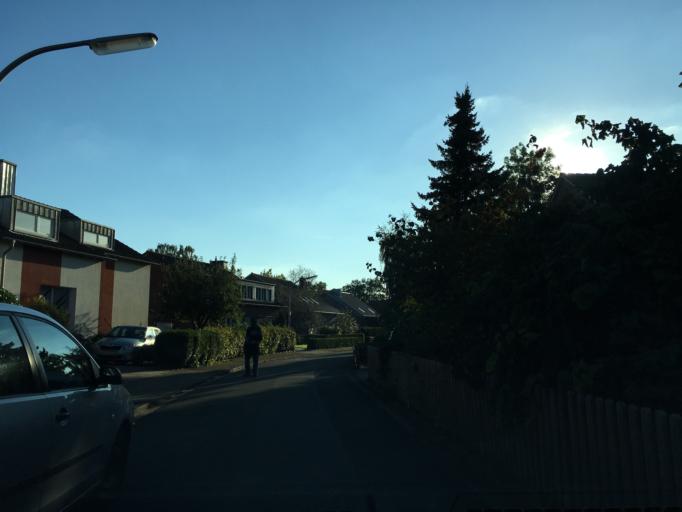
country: DE
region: North Rhine-Westphalia
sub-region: Regierungsbezirk Munster
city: Muenster
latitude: 51.9973
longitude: 7.5620
